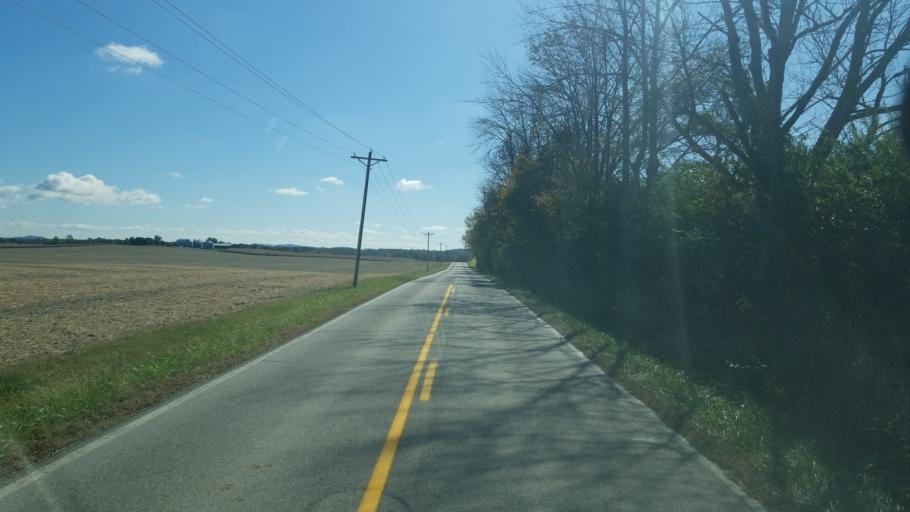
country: US
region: Ohio
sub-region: Highland County
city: Leesburg
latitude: 39.2859
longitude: -83.5016
